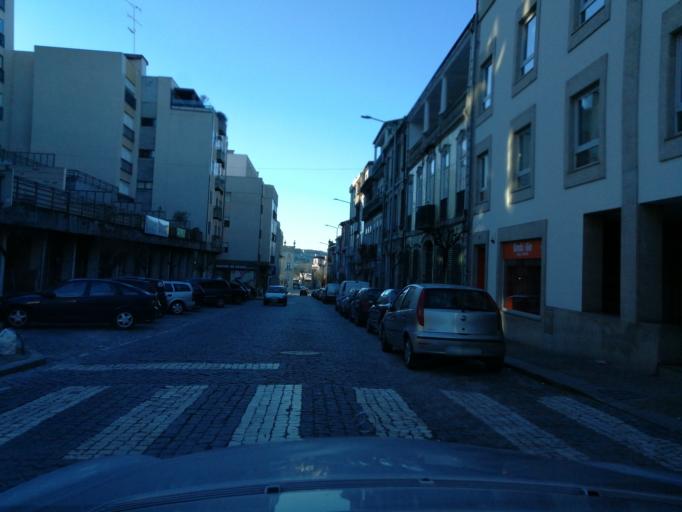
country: PT
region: Braga
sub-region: Braga
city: Braga
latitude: 41.5534
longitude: -8.4170
